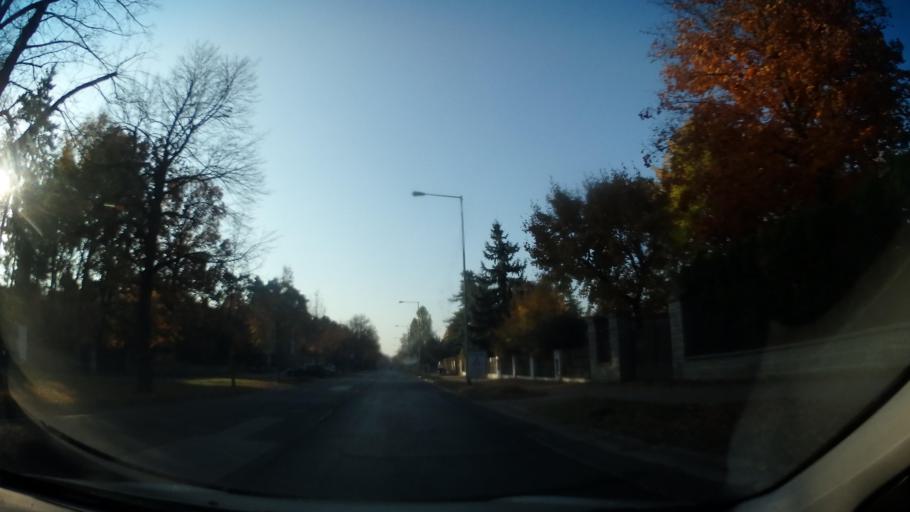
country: CZ
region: Central Bohemia
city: Sestajovice
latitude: 50.0926
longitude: 14.6678
